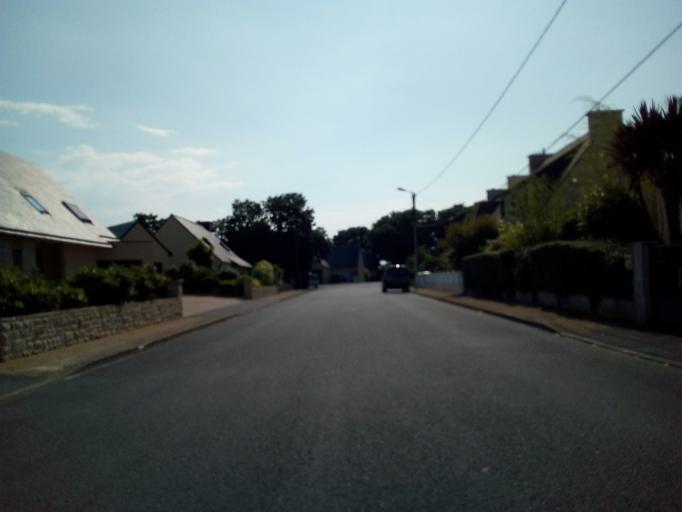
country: FR
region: Brittany
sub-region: Departement du Finistere
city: Landivisiau
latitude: 48.5083
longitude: -4.0624
